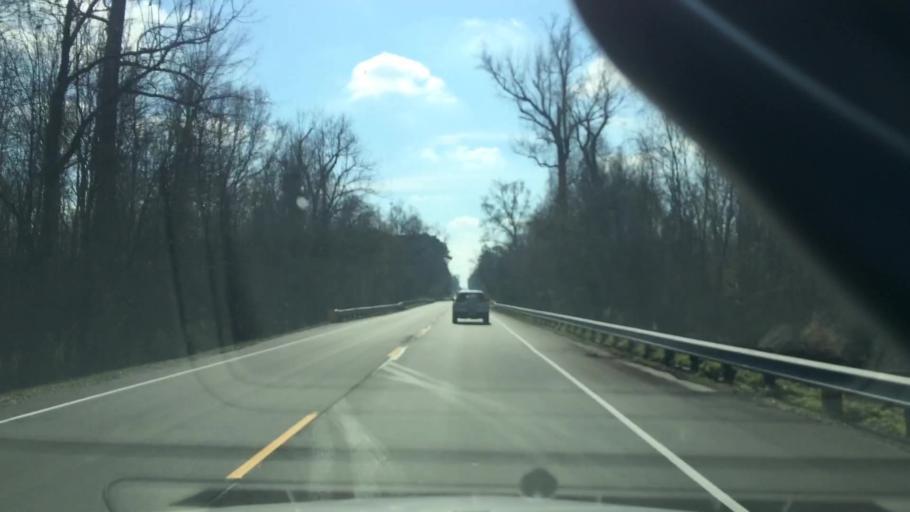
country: US
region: North Carolina
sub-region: Duplin County
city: Beulaville
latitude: 34.9432
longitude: -77.7689
